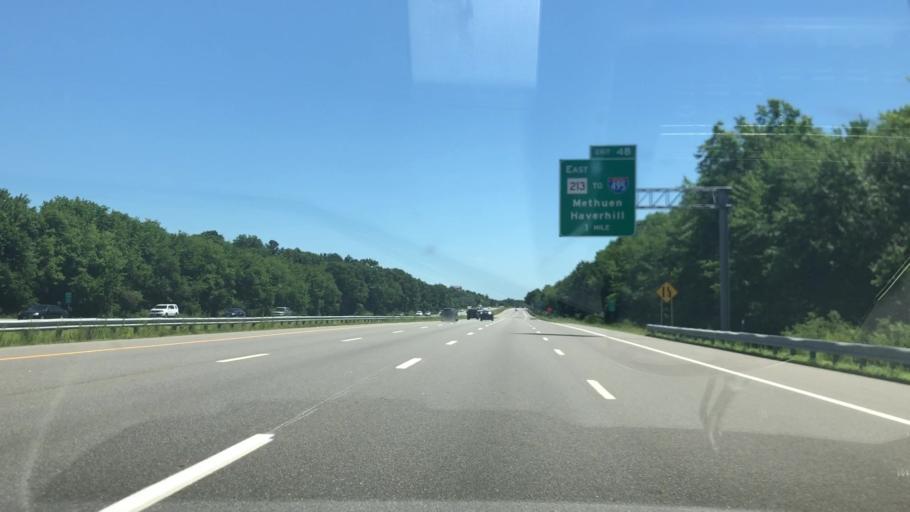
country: US
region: Massachusetts
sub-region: Essex County
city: Methuen
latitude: 42.7509
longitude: -71.2178
